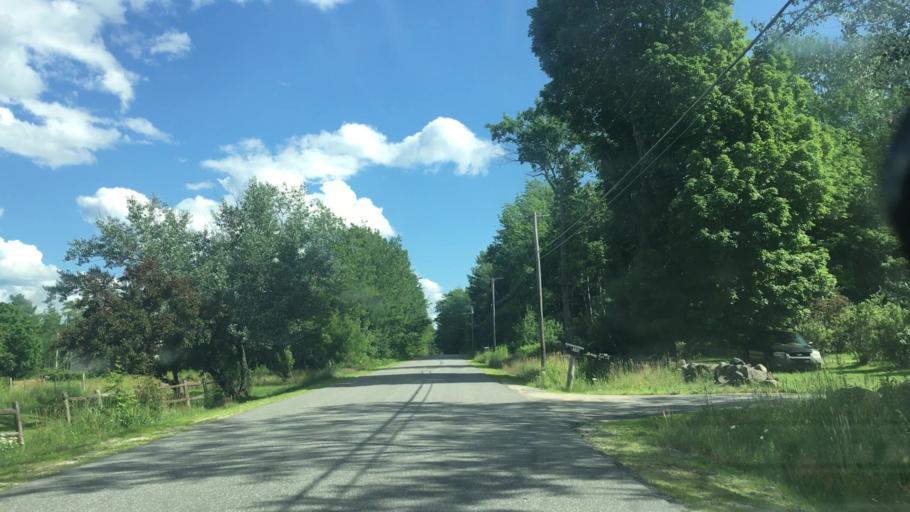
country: US
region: Maine
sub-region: Franklin County
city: Wilton
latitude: 44.6386
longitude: -70.1999
